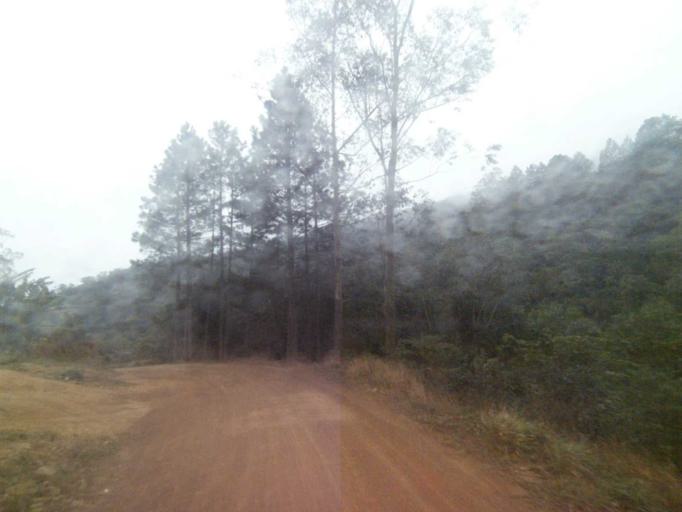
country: BR
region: Santa Catarina
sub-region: Anitapolis
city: Anitapolis
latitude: -27.8896
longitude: -49.1317
